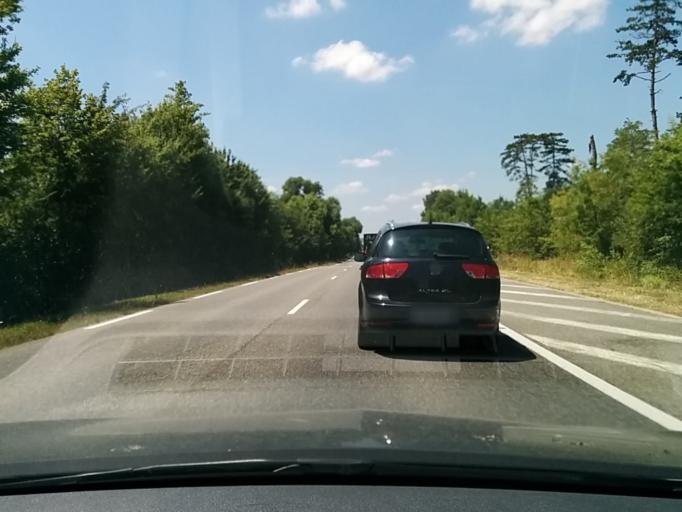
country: FR
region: Midi-Pyrenees
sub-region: Departement du Gers
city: Auch
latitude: 43.6764
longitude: 0.5158
